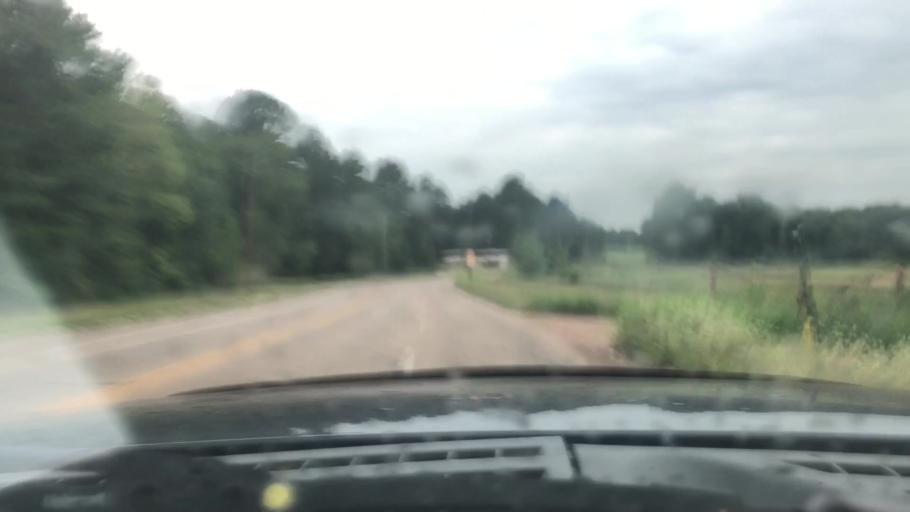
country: US
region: Texas
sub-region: Bowie County
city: Wake Village
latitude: 33.4081
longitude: -94.0797
